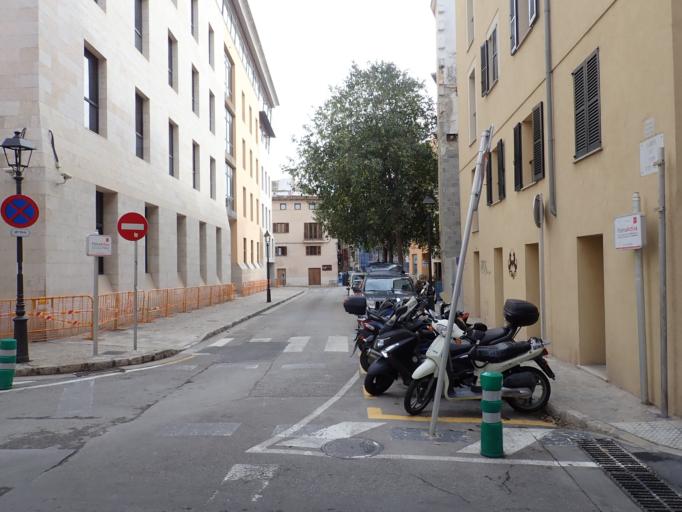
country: ES
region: Balearic Islands
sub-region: Illes Balears
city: Palma
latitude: 39.5703
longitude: 2.6548
